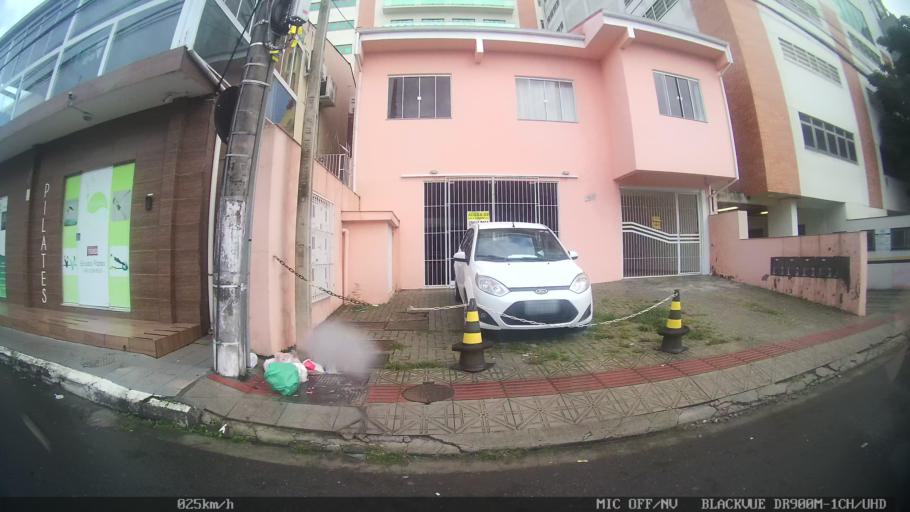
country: BR
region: Santa Catarina
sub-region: Sao Jose
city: Campinas
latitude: -27.5872
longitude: -48.6110
